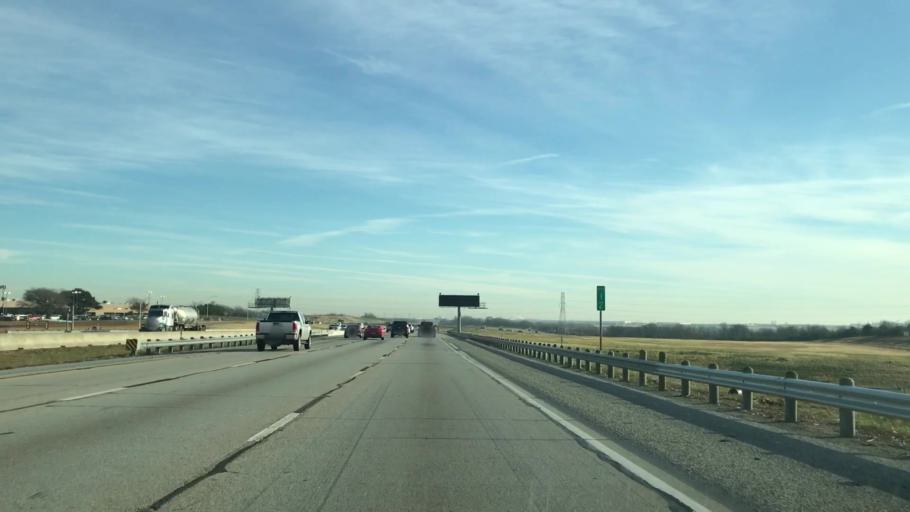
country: US
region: Texas
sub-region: Tarrant County
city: Sansom Park
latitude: 32.8259
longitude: -97.3864
